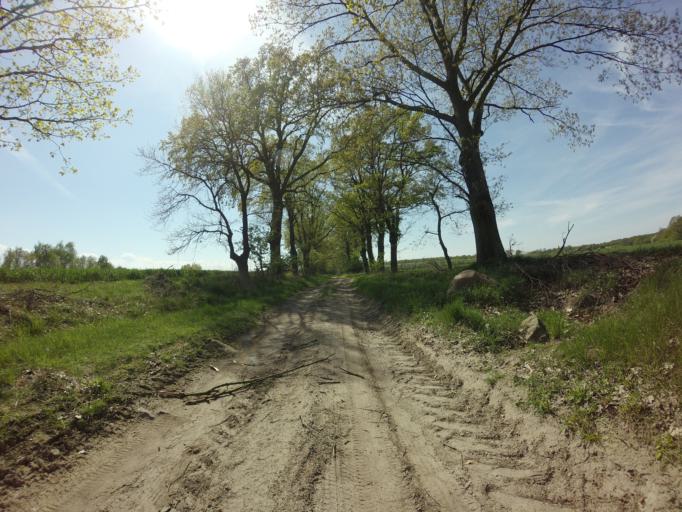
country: PL
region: West Pomeranian Voivodeship
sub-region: Powiat choszczenski
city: Choszczno
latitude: 53.1607
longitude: 15.3416
